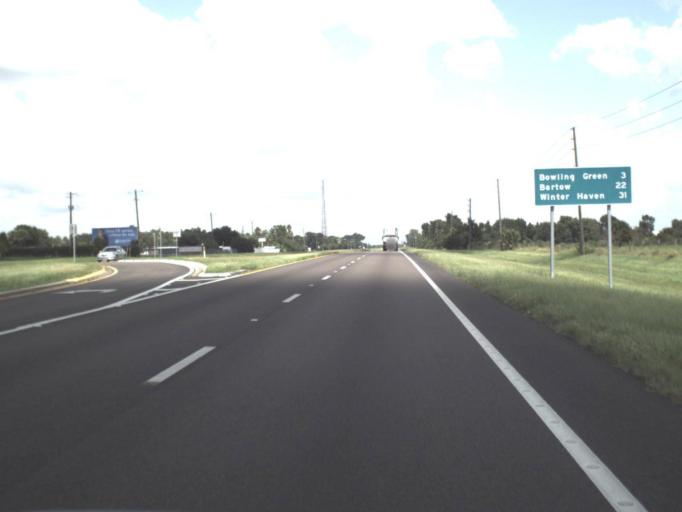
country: US
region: Florida
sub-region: Hardee County
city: Bowling Green
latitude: 27.5970
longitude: -81.8224
